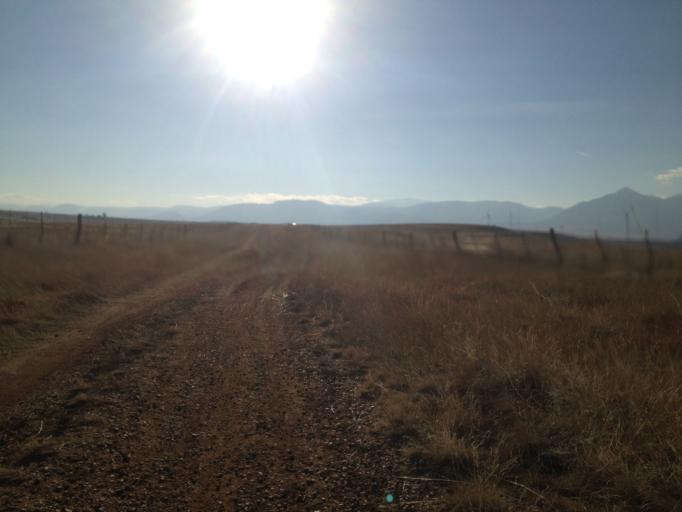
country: US
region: Colorado
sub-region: Boulder County
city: Superior
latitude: 39.9201
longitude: -105.1958
